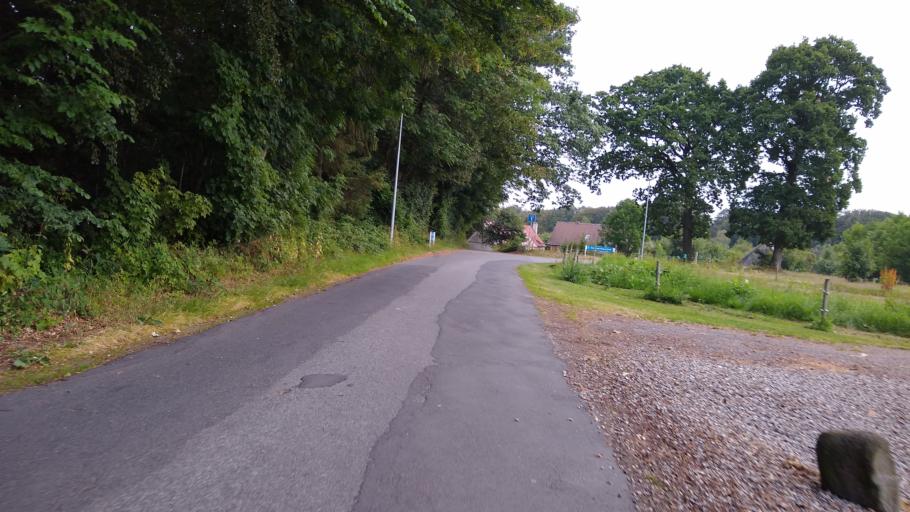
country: DK
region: South Denmark
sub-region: Vejle Kommune
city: Brejning
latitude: 55.6612
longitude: 9.6647
